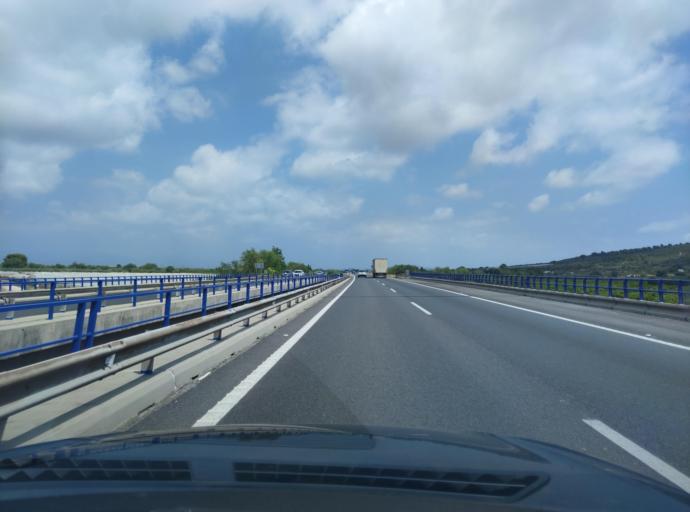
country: ES
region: Valencia
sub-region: Provincia de Castello
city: Vinaros
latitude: 40.5018
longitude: 0.4160
